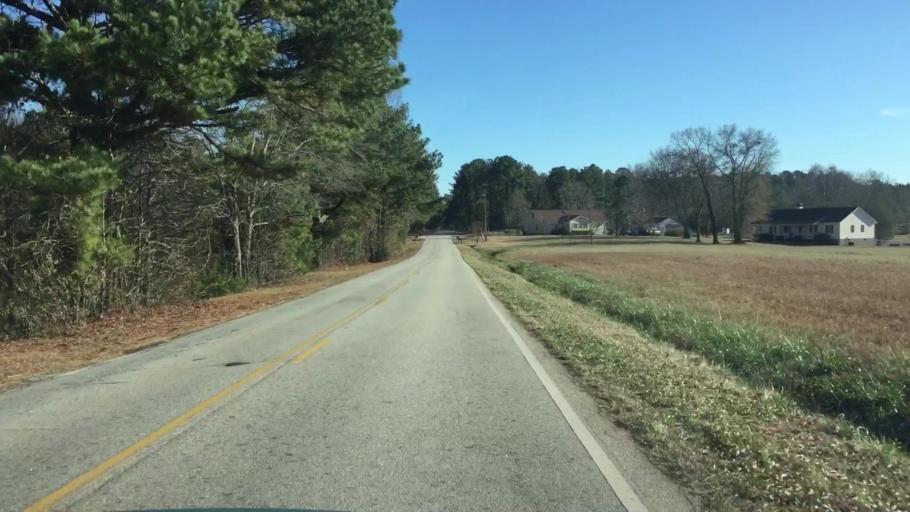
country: US
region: Georgia
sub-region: Newton County
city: Oakwood
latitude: 33.4726
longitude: -84.0178
